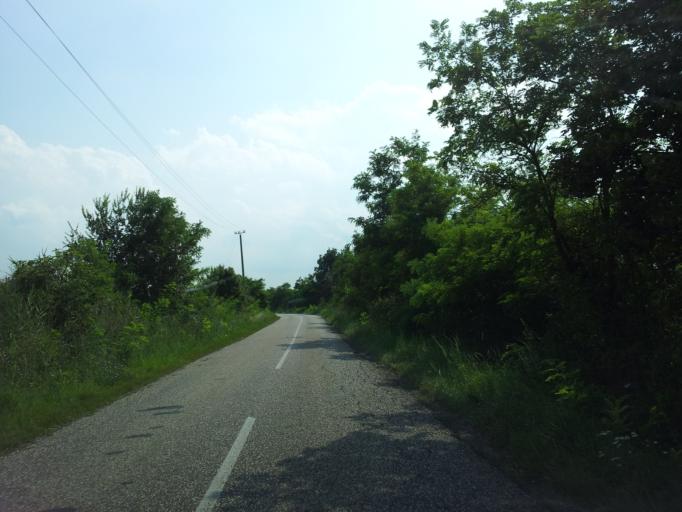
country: HU
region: Pest
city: Szigetujfalu
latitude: 47.2157
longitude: 18.9197
